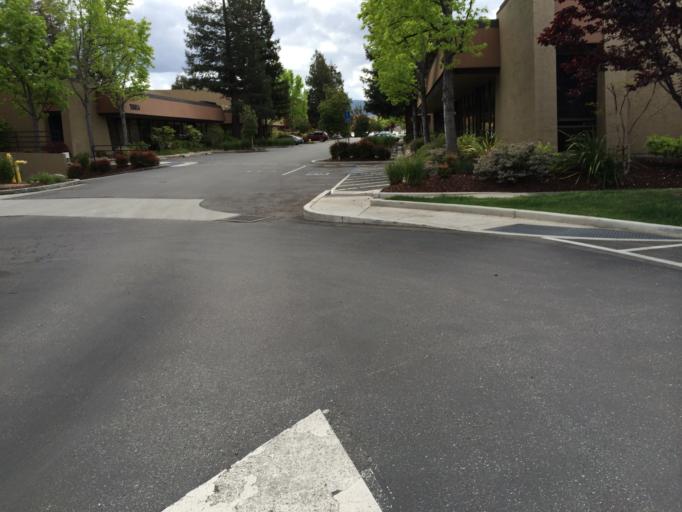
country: US
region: California
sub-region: Santa Clara County
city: Cupertino
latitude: 37.3250
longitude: -122.0384
